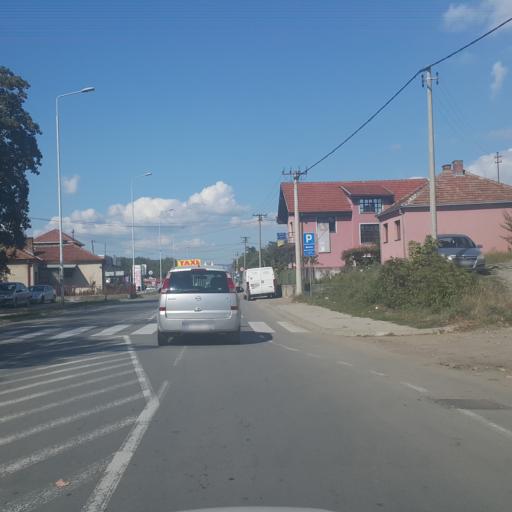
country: RS
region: Central Serbia
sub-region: Pirotski Okrug
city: Pirot
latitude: 43.1720
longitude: 22.5835
